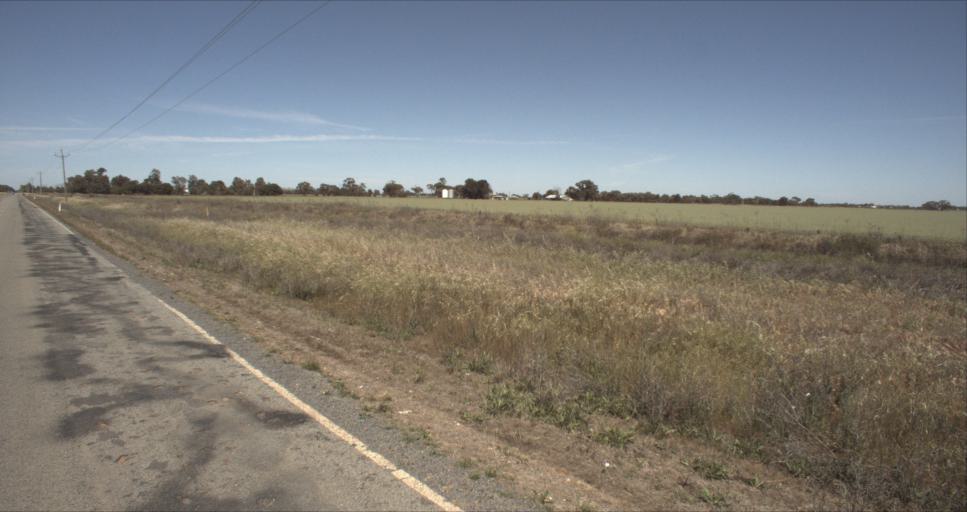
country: AU
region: New South Wales
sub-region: Leeton
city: Leeton
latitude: -34.5095
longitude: 146.2854
